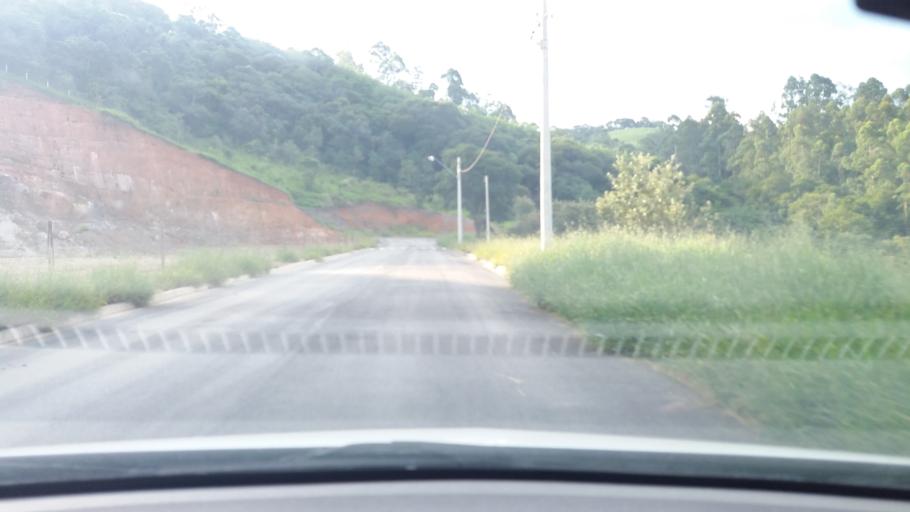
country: BR
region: Sao Paulo
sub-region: Bom Jesus Dos Perdoes
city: Bom Jesus dos Perdoes
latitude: -23.1511
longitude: -46.4759
